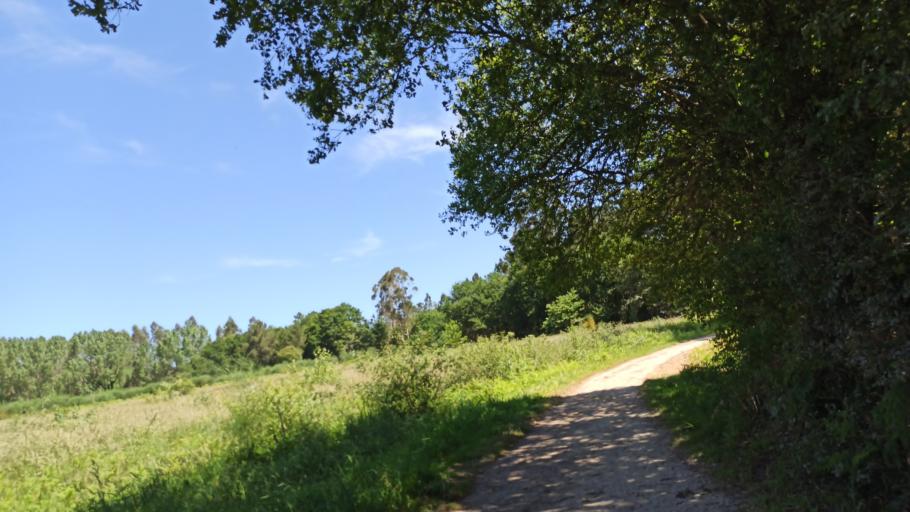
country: ES
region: Galicia
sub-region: Provincia da Coruna
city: Negreira
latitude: 42.9141
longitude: -8.7312
